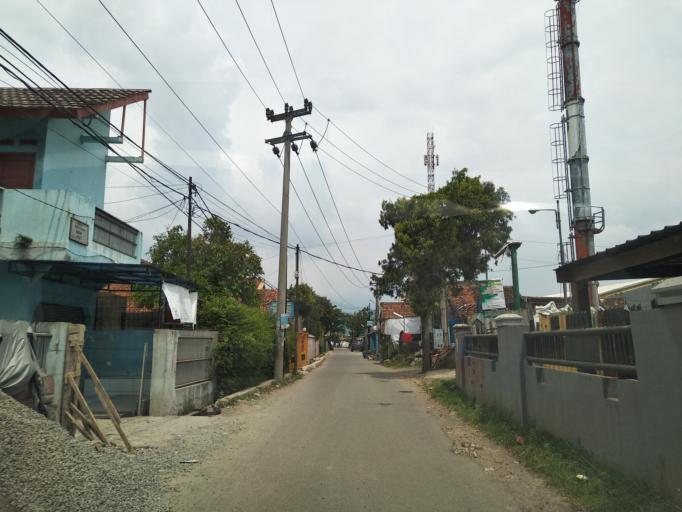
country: ID
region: West Java
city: Pameungpeuk
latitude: -6.9745
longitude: 107.6475
